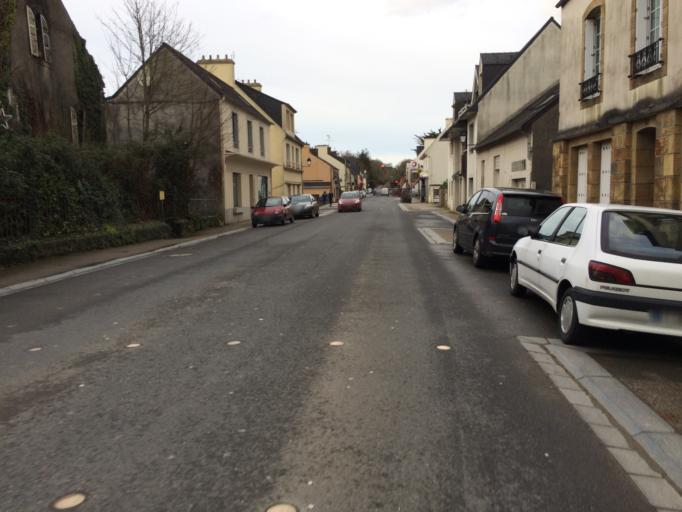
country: FR
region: Brittany
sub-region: Departement du Finistere
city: Daoulas
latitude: 48.3600
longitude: -4.2598
